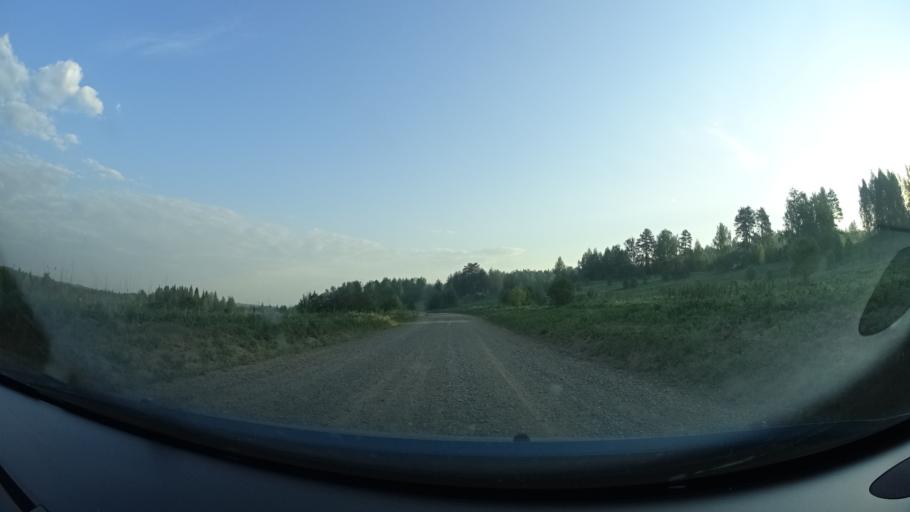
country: RU
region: Perm
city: Kuyeda
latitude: 56.6417
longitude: 55.7064
